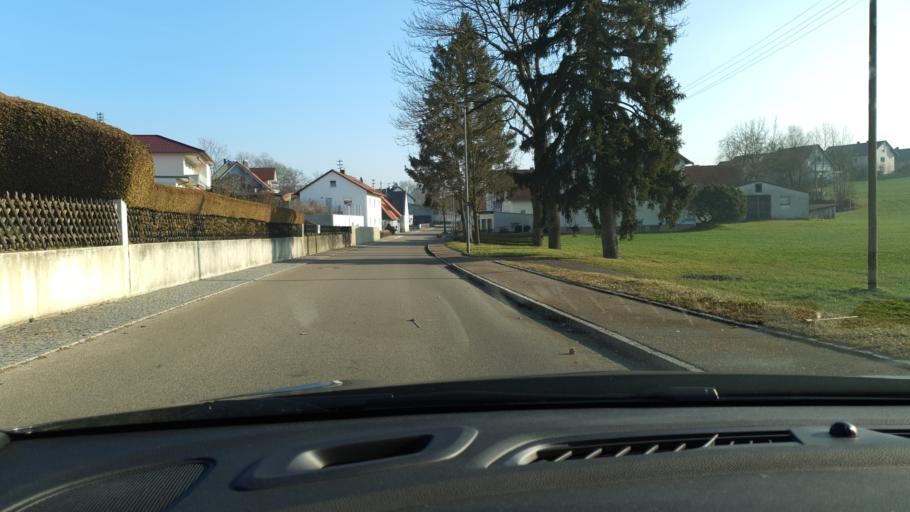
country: DE
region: Bavaria
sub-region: Swabia
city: Burgau
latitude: 48.4329
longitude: 10.3897
